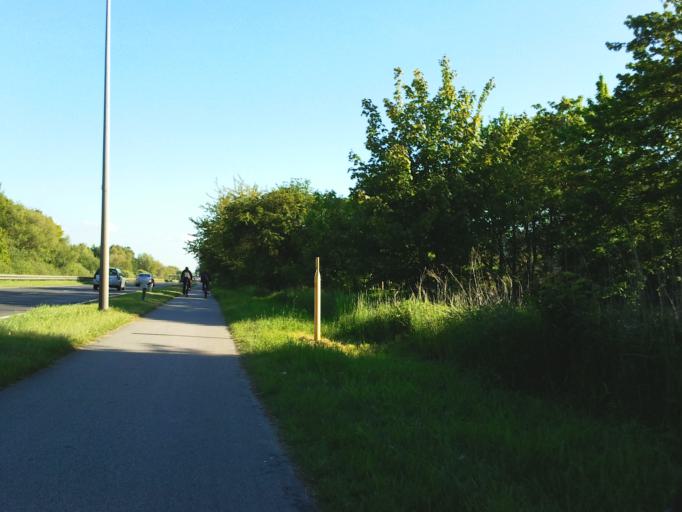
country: DE
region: Mecklenburg-Vorpommern
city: Warnemuende
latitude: 54.1295
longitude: 12.0636
